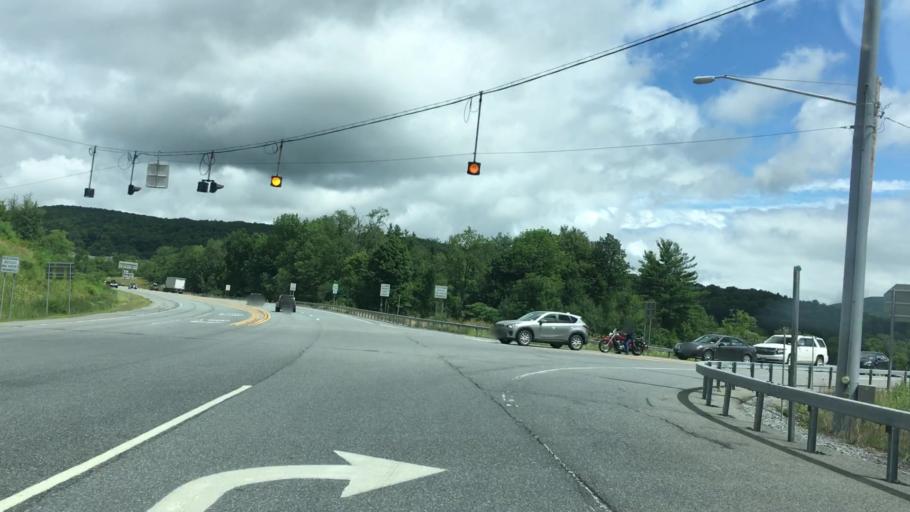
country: US
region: New York
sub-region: Rensselaer County
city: Hoosick Falls
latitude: 42.8794
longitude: -73.2911
